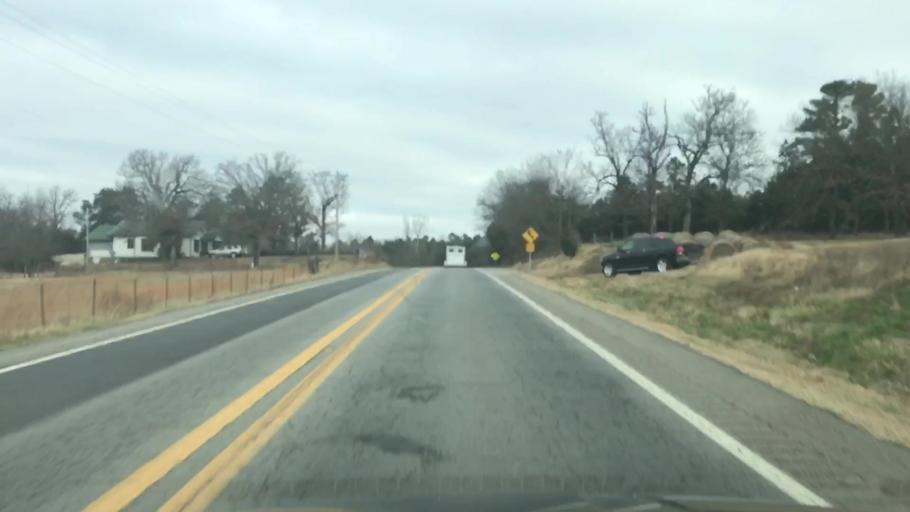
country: US
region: Arkansas
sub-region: Scott County
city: Waldron
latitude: 34.9493
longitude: -94.1049
